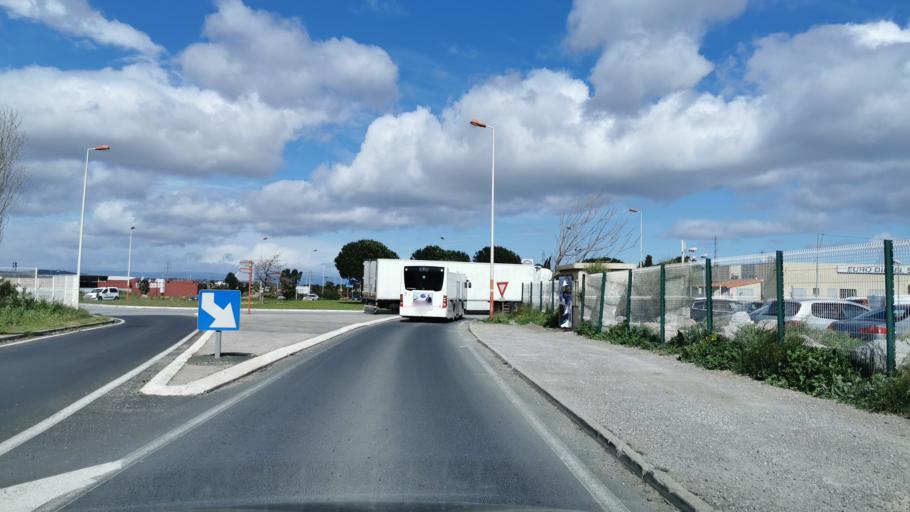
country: FR
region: Languedoc-Roussillon
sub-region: Departement de l'Aude
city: Narbonne
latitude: 43.1618
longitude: 2.9889
